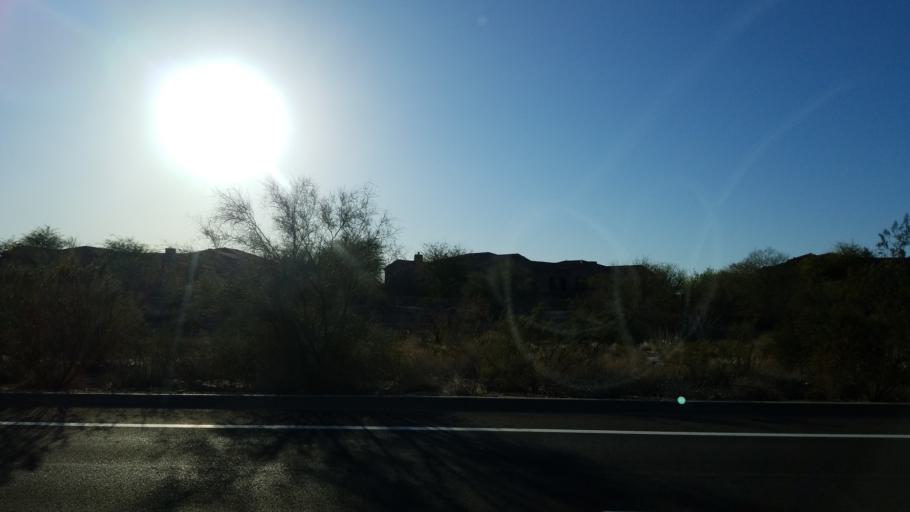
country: US
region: Arizona
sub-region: Maricopa County
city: Paradise Valley
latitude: 33.6676
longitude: -111.8907
